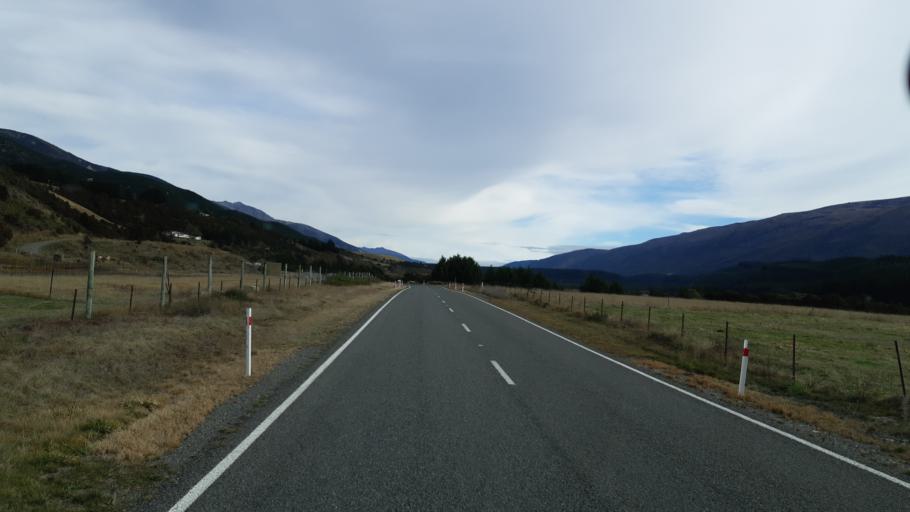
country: NZ
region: Tasman
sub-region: Tasman District
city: Wakefield
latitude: -41.6879
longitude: 173.1555
